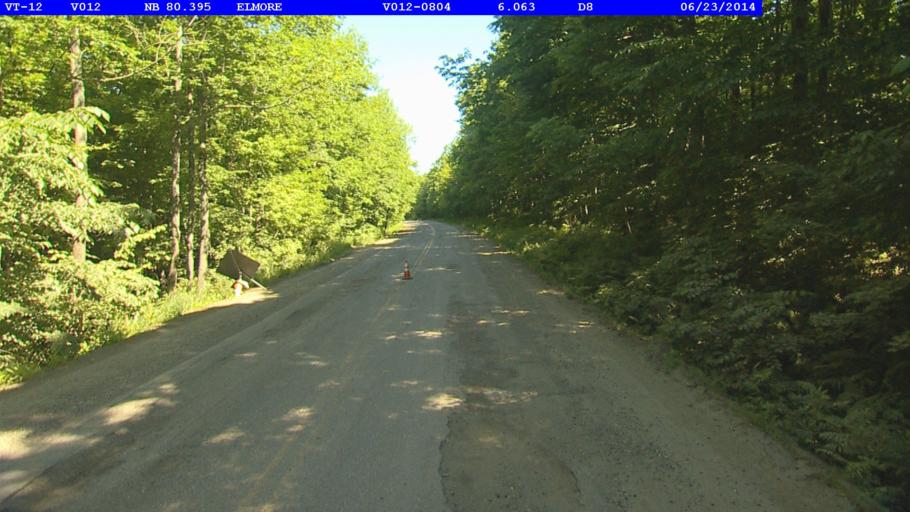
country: US
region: Vermont
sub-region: Lamoille County
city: Morrisville
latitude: 44.5316
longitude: -72.5185
